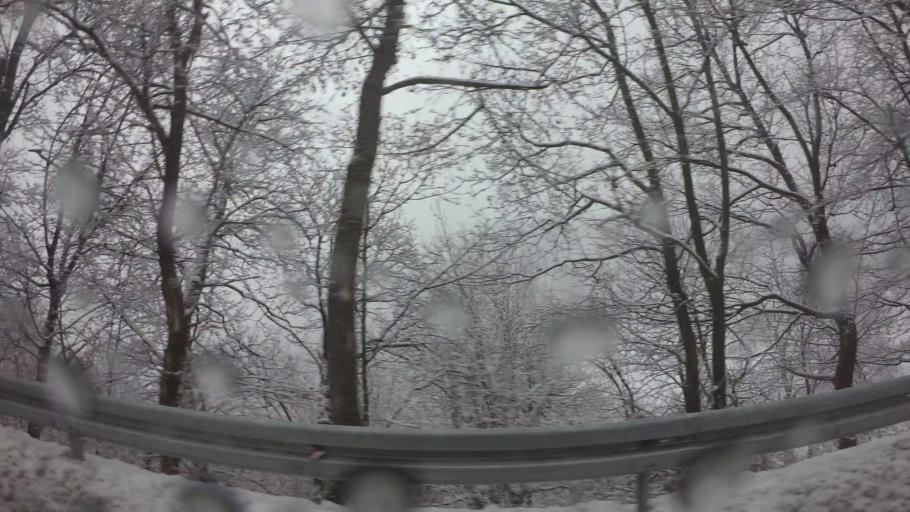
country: BA
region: Federation of Bosnia and Herzegovina
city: Kobilja Glava
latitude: 43.8517
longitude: 18.4510
